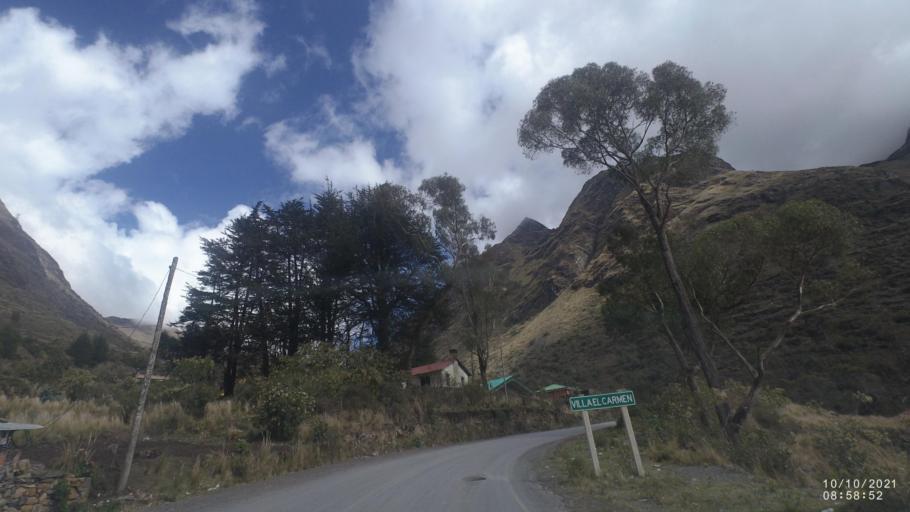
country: BO
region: La Paz
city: Quime
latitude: -16.9974
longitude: -67.2590
